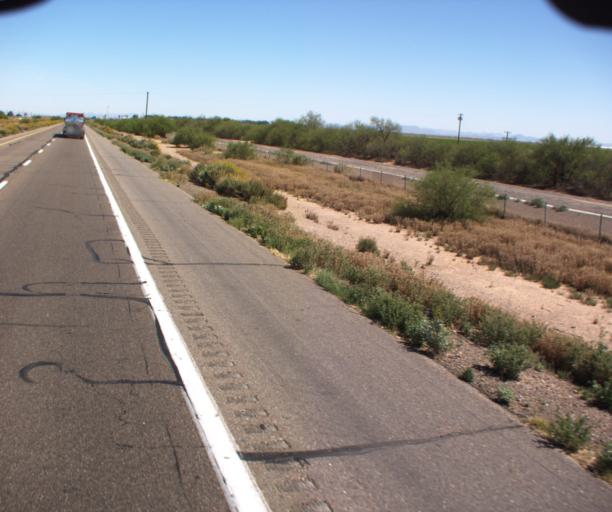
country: US
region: Arizona
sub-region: Maricopa County
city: Gila Bend
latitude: 32.9171
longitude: -112.9154
